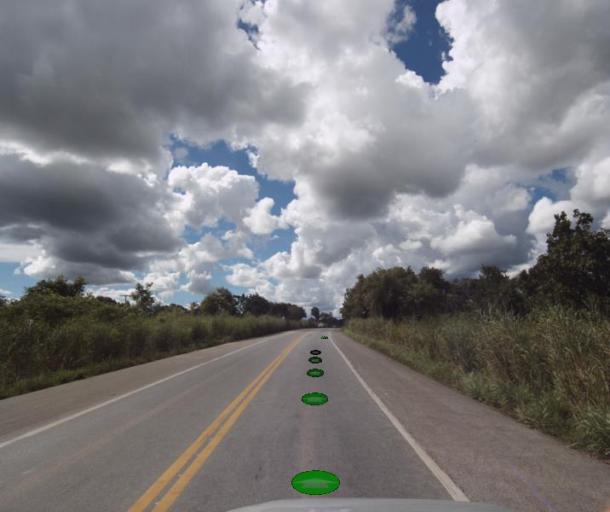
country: BR
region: Goias
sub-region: Porangatu
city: Porangatu
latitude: -13.4113
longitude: -49.1317
